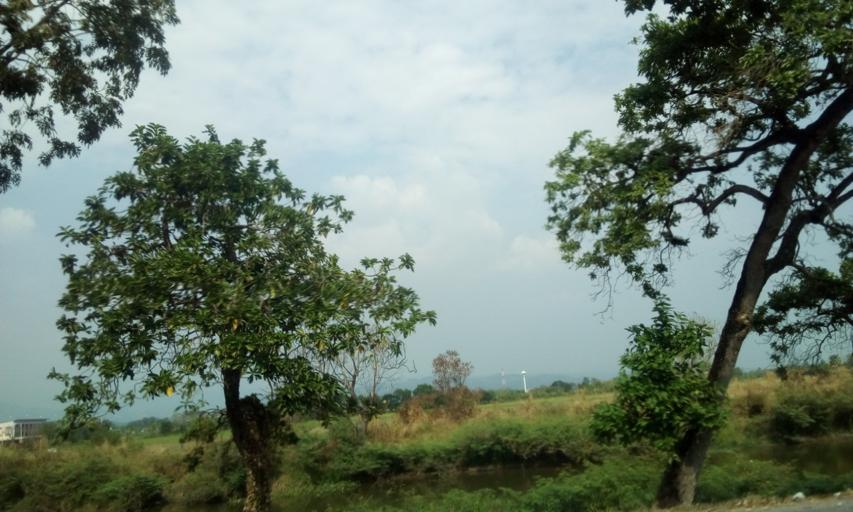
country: TH
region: Nakhon Nayok
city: Nakhon Nayok
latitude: 14.2130
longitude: 101.1741
